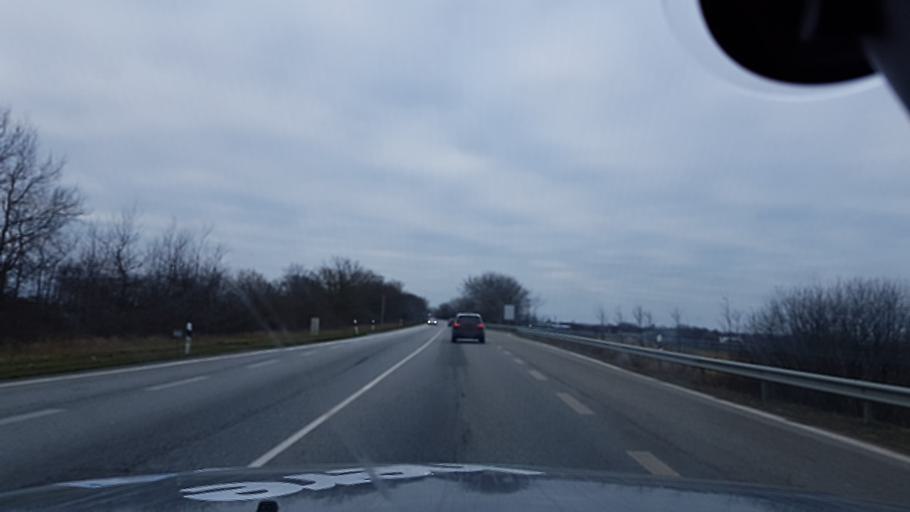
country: DE
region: Schleswig-Holstein
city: Grossenbrode
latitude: 54.4244
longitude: 11.1302
